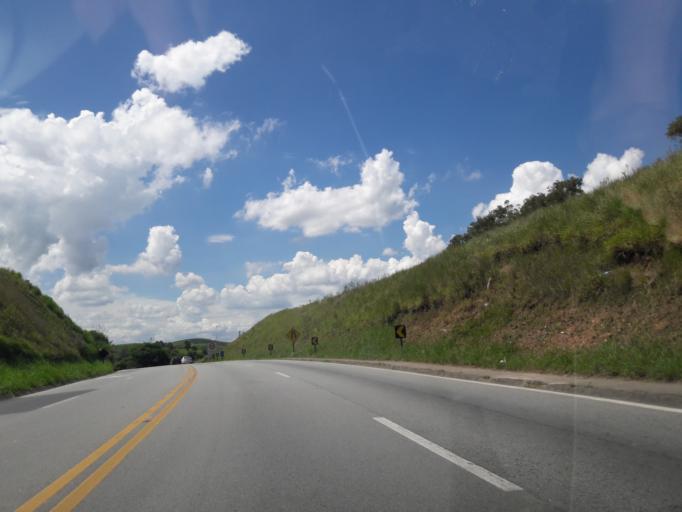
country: BR
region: Sao Paulo
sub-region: Cajamar
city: Cajamar
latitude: -23.3387
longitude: -46.8244
